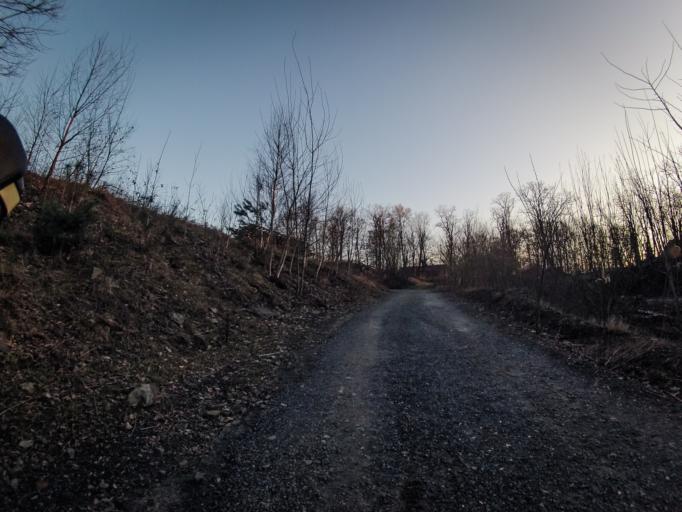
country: DE
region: Lower Saxony
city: Wallenhorst
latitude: 52.3134
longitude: 8.0043
